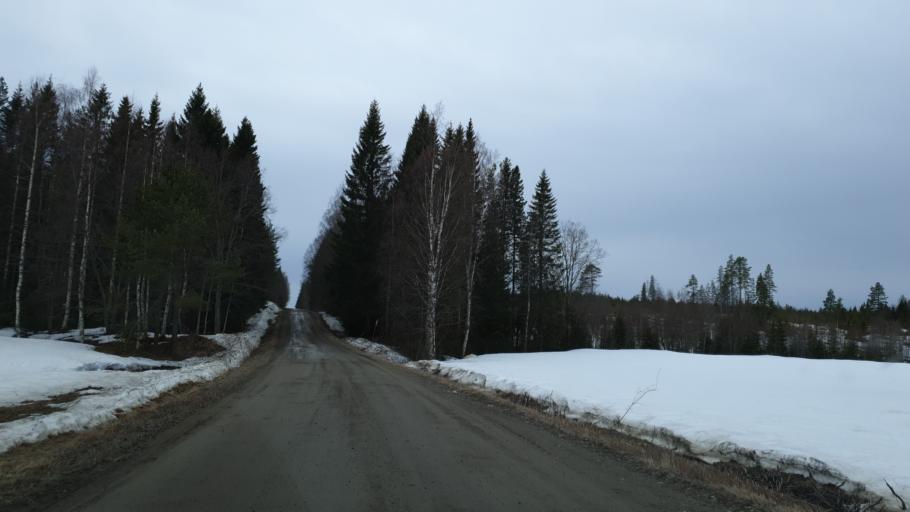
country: SE
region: Vaesterbotten
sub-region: Robertsfors Kommun
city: Robertsfors
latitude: 64.3951
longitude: 21.0009
